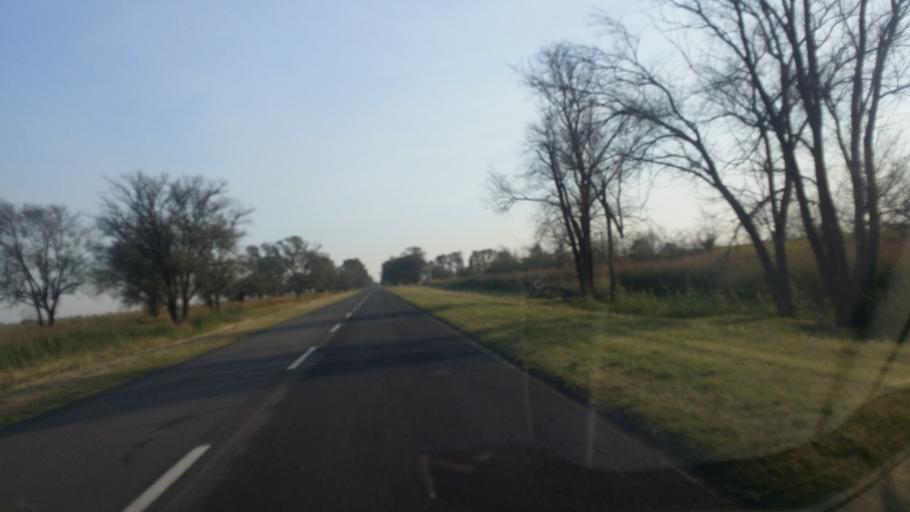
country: AR
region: La Pampa
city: Winifreda
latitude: -36.1927
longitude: -64.2779
